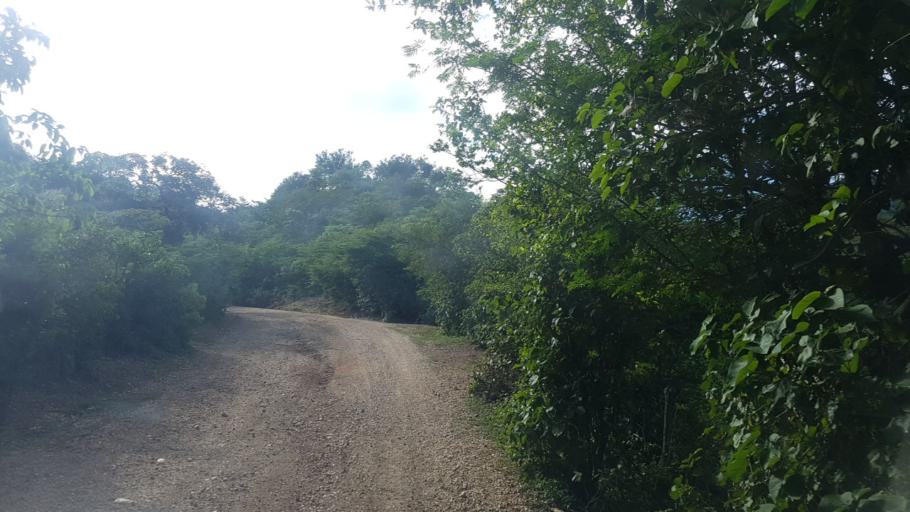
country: NI
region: Nueva Segovia
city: Ocotal
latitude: 13.6079
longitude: -86.4472
